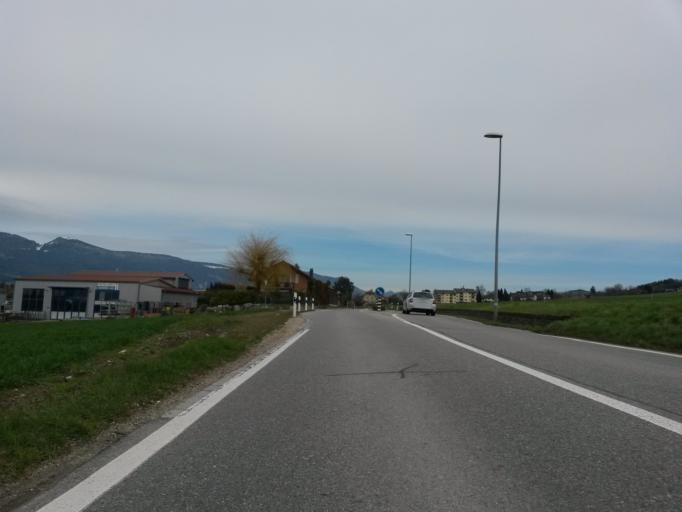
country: CH
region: Bern
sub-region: Seeland District
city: Arch
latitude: 47.1611
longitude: 7.4182
